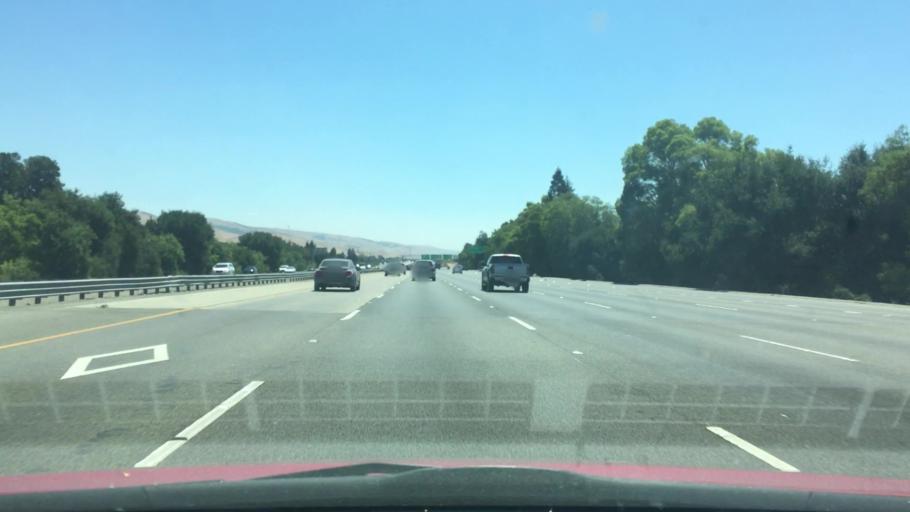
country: US
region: California
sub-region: Santa Clara County
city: Seven Trees
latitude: 37.2510
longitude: -121.7855
